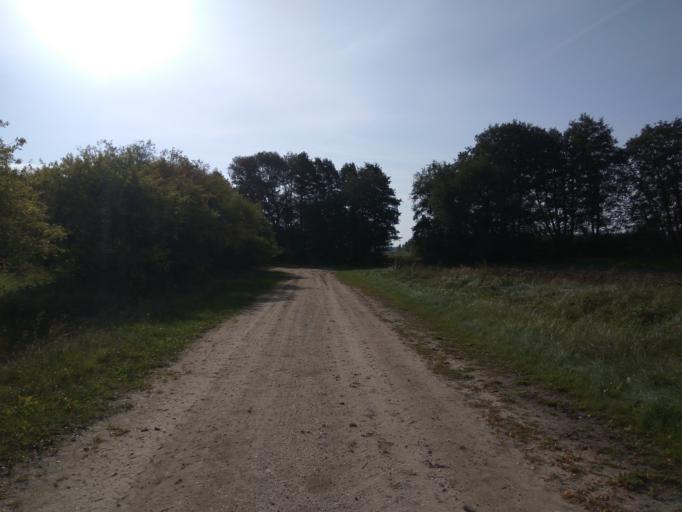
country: LV
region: Ventspils
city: Ventspils
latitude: 57.3552
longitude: 21.6392
